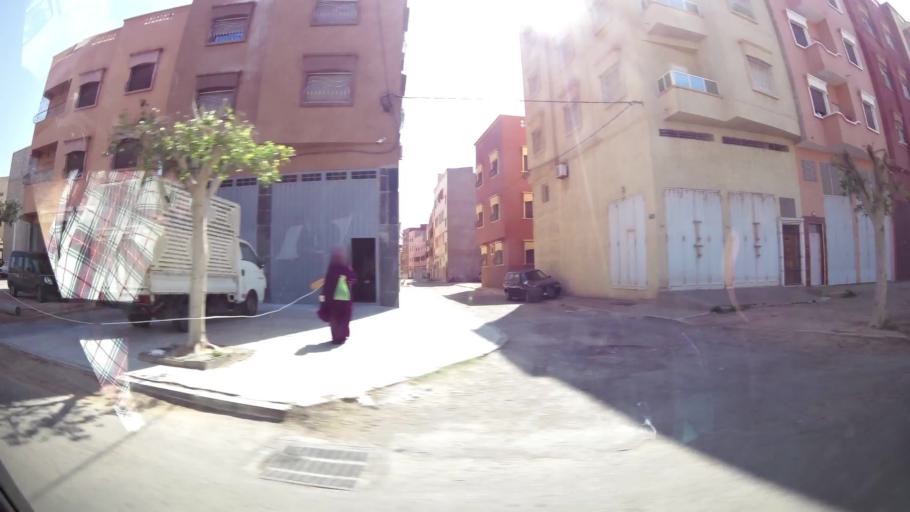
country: MA
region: Souss-Massa-Draa
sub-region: Inezgane-Ait Mellou
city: Inezgane
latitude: 30.3446
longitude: -9.5077
